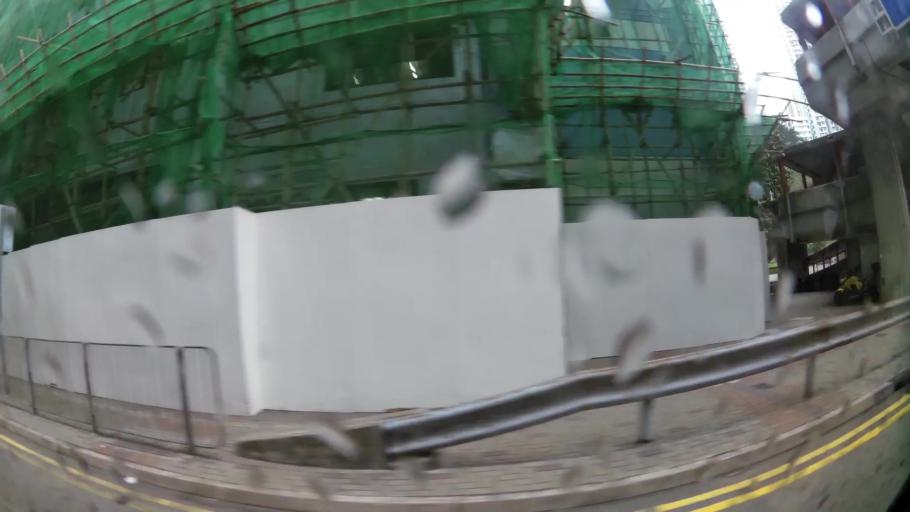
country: HK
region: Tsuen Wan
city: Tsuen Wan
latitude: 22.3657
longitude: 114.1202
